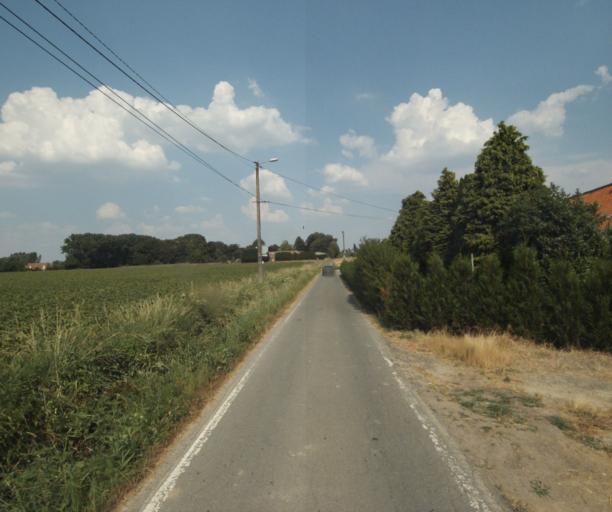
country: FR
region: Nord-Pas-de-Calais
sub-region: Departement du Nord
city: Linselles
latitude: 50.7292
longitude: 3.0615
